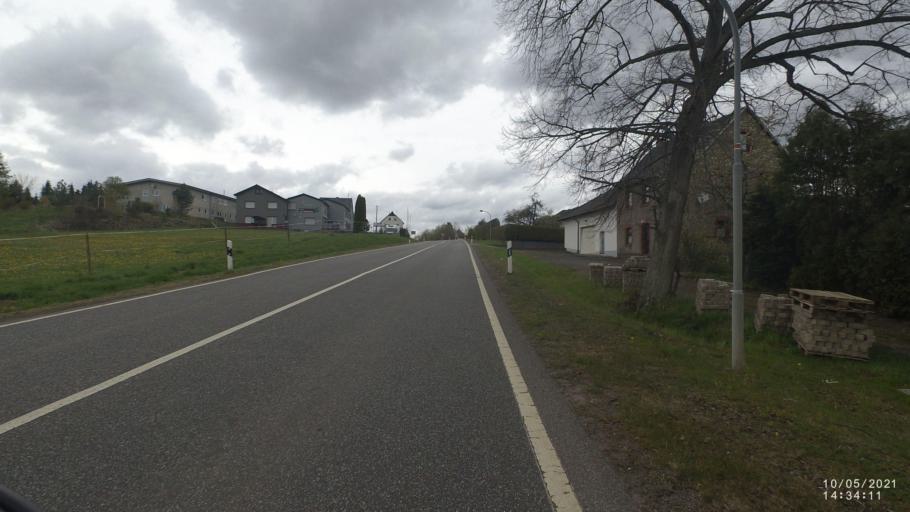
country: DE
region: Rheinland-Pfalz
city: Nitz
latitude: 50.3496
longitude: 7.0315
